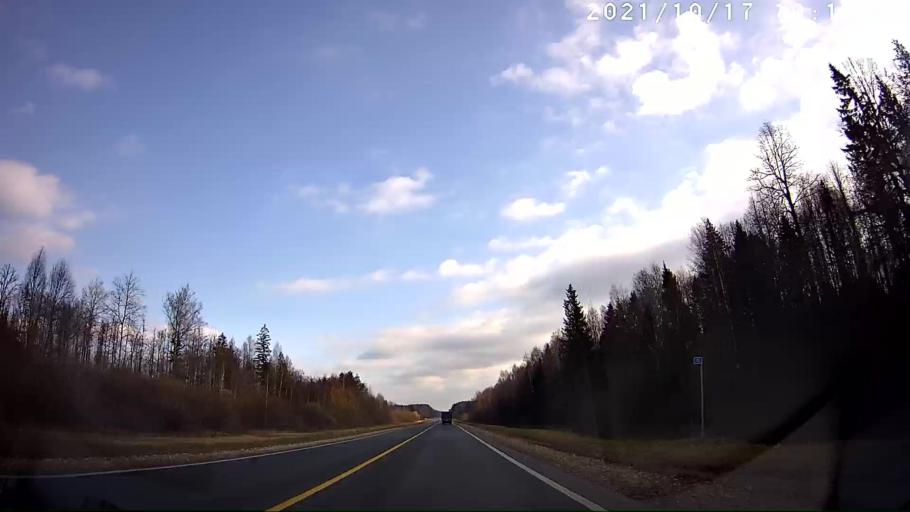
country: RU
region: Mariy-El
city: Sovetskiy
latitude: 56.7397
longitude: 48.4112
